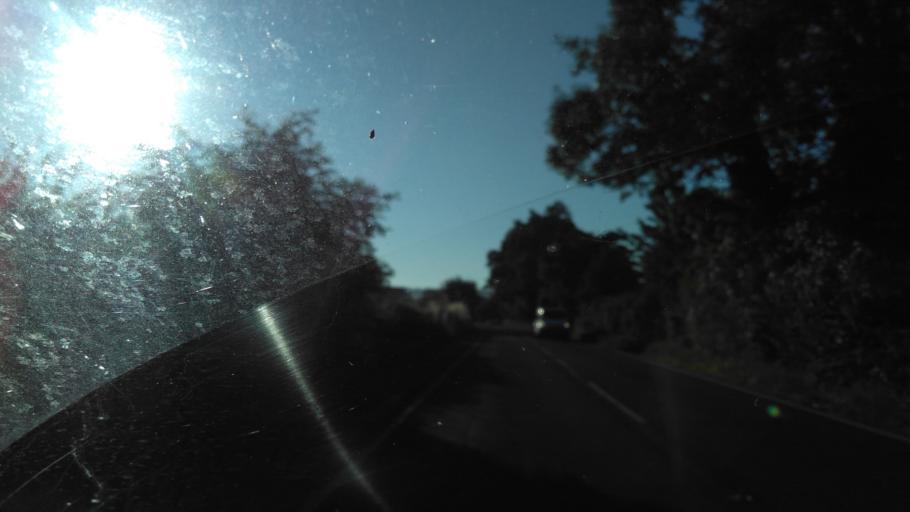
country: GB
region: England
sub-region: Kent
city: Chartham
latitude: 51.2584
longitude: 1.0143
